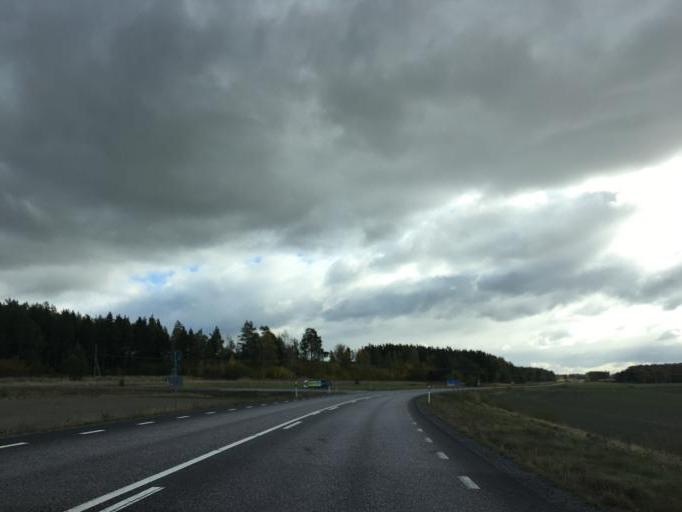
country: SE
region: Soedermanland
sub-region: Nykopings Kommun
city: Olstorp
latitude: 58.8950
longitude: 16.6499
